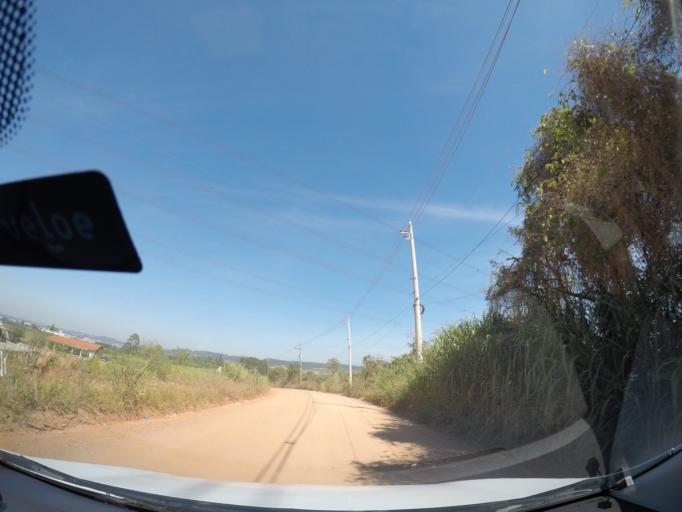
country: BR
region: Sao Paulo
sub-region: Itupeva
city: Itupeva
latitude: -23.1229
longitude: -47.0079
